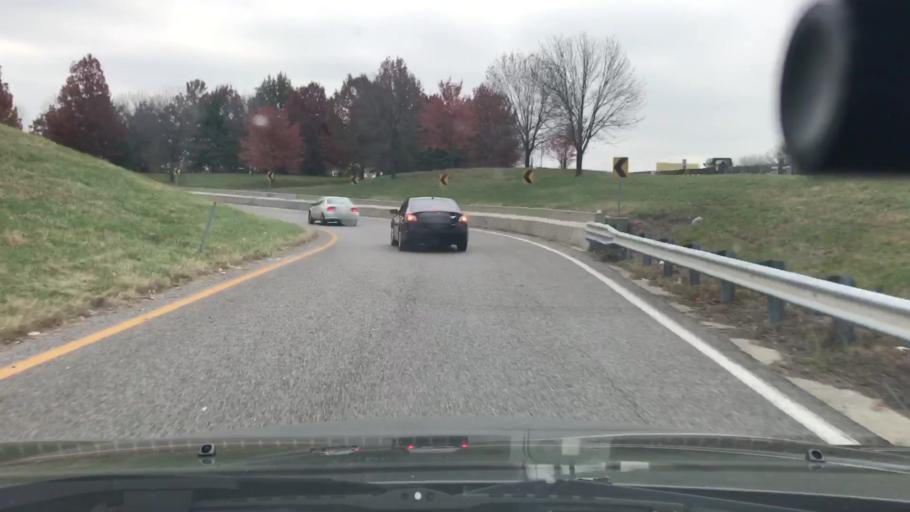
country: US
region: Missouri
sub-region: City of Saint Louis
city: St. Louis
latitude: 38.6114
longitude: -90.2127
